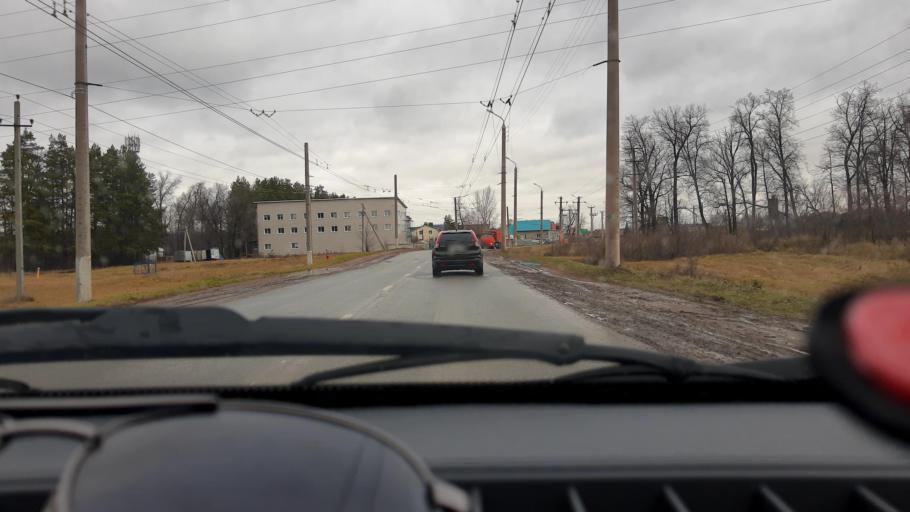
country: RU
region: Bashkortostan
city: Ufa
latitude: 54.7809
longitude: 55.9480
